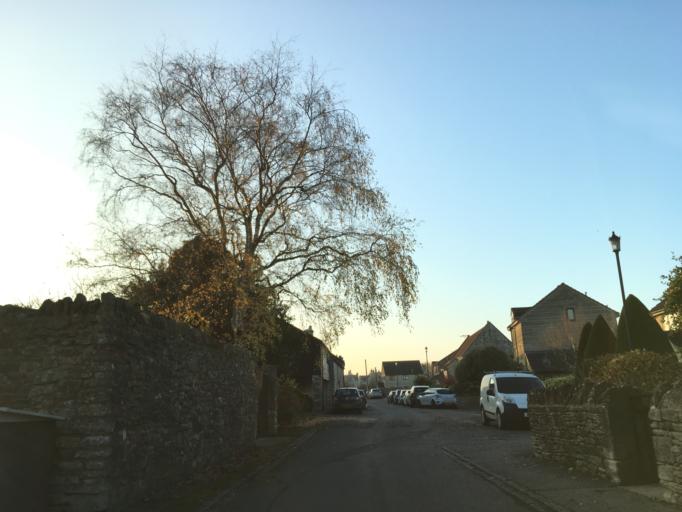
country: GB
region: England
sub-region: South Gloucestershire
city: Marshfield
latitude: 51.4630
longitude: -2.3187
